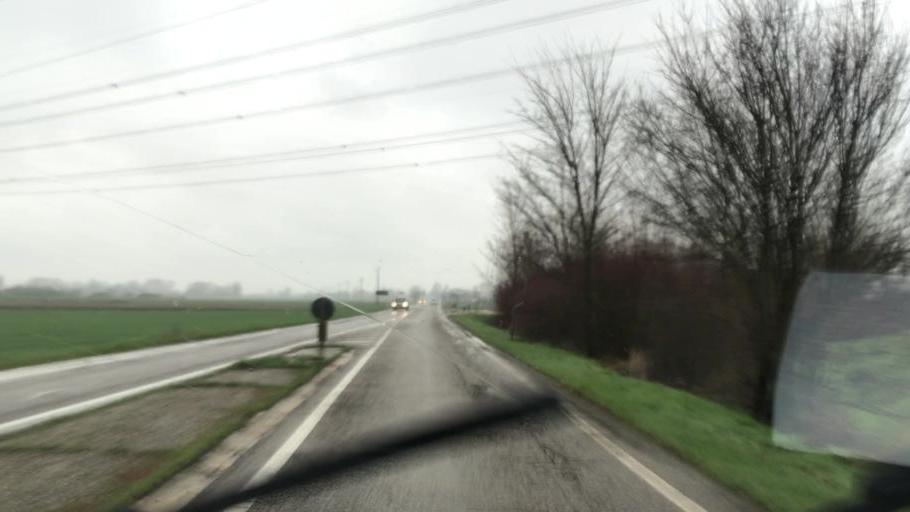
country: IT
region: Lombardy
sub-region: Provincia di Mantova
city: Carbonara di Po
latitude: 45.0216
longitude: 11.2496
